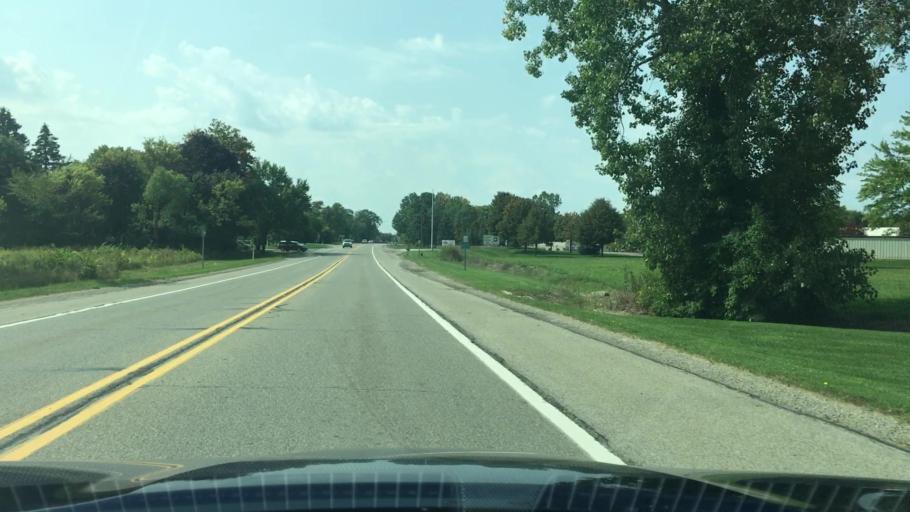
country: US
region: Michigan
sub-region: Washtenaw County
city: Ypsilanti
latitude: 42.2133
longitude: -83.6721
